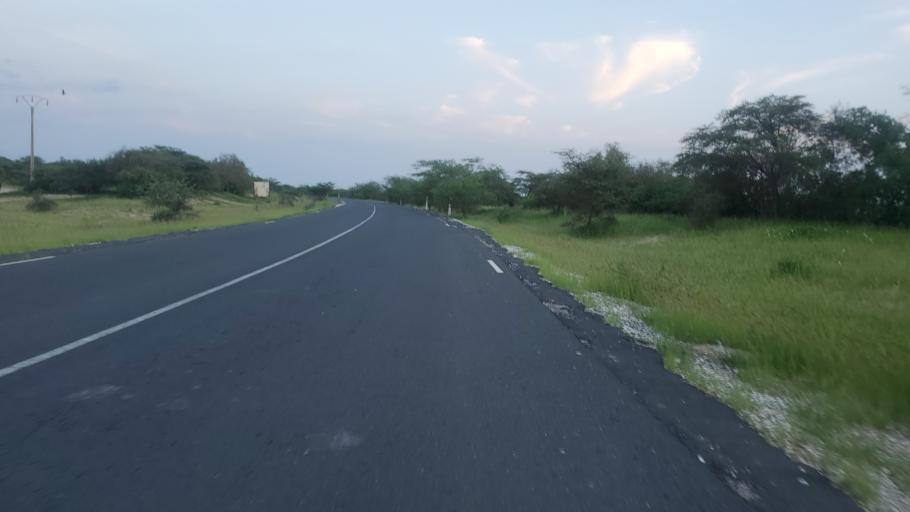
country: SN
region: Saint-Louis
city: Saint-Louis
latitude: 16.1033
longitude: -16.4114
